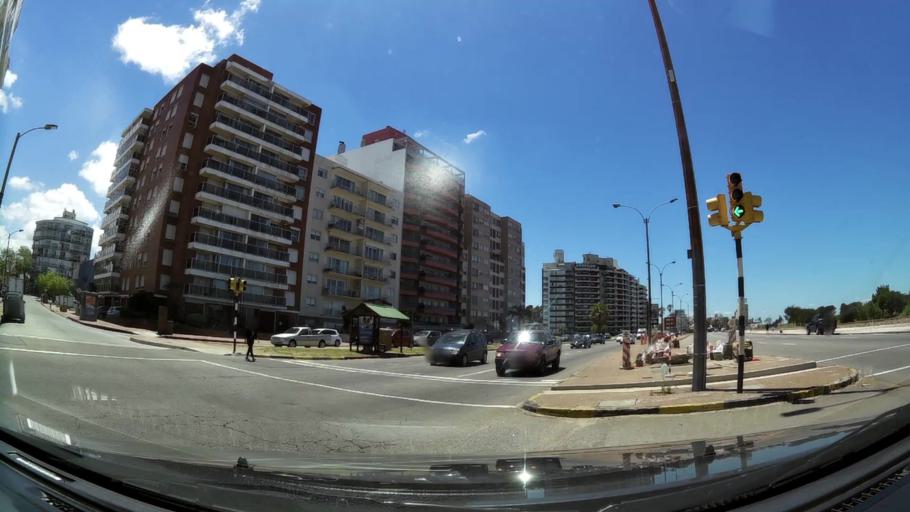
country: UY
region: Canelones
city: Paso de Carrasco
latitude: -34.8958
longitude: -56.1080
